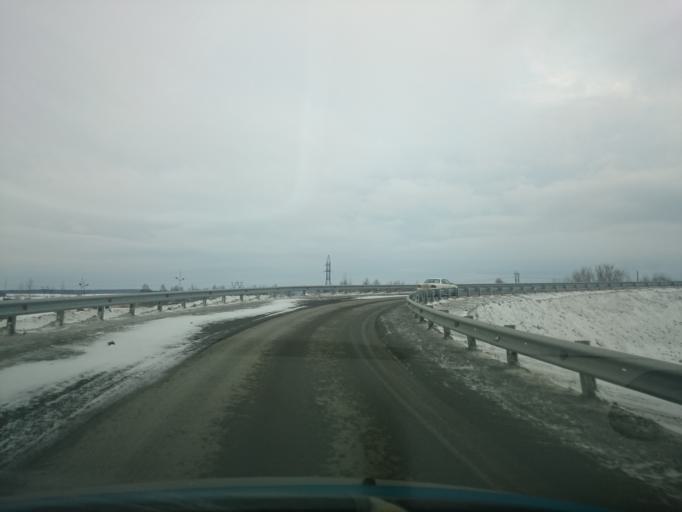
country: RU
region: Sverdlovsk
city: Achit
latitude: 56.7895
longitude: 57.8842
